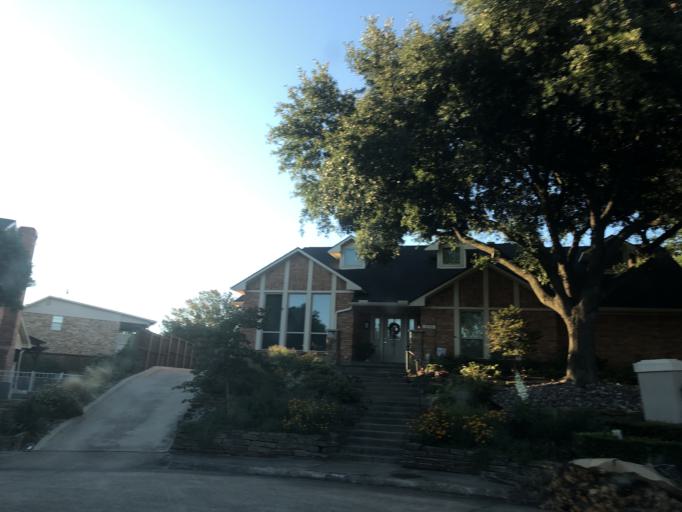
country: US
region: Texas
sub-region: Dallas County
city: Garland
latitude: 32.8418
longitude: -96.6398
